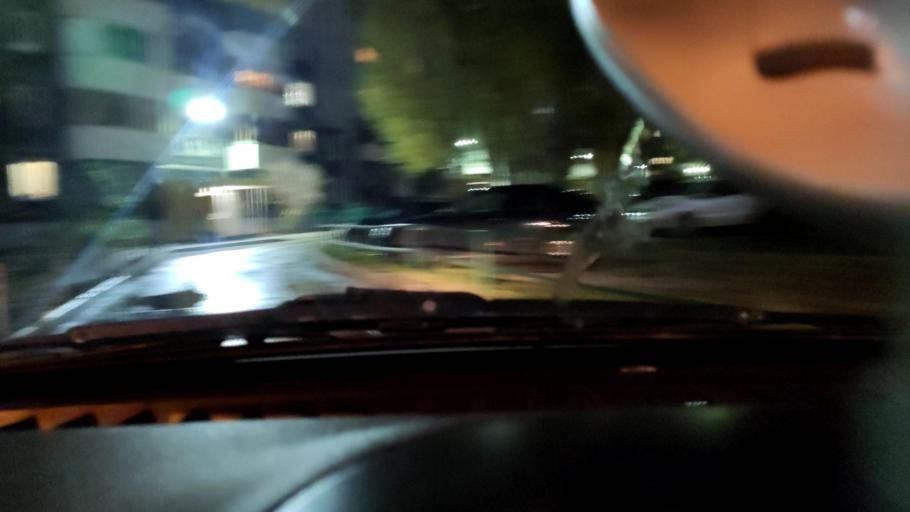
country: RU
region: Perm
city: Perm
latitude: 58.0110
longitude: 56.3117
